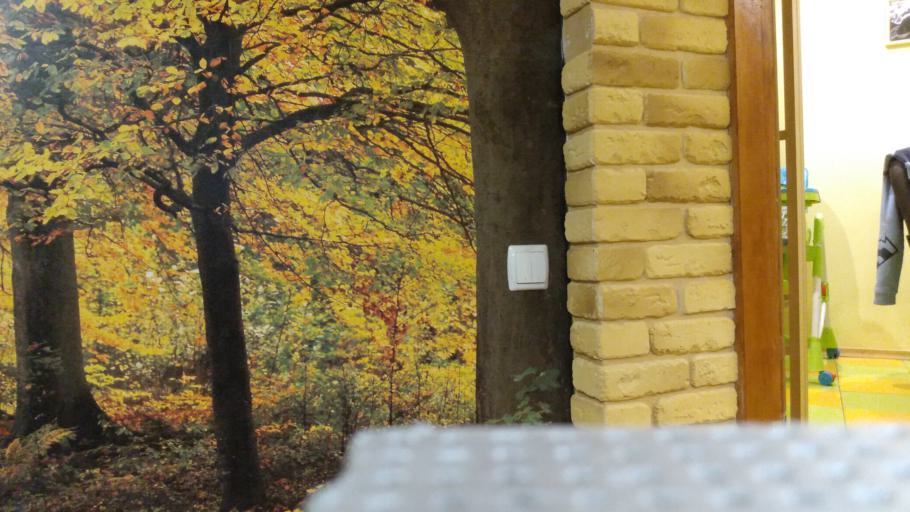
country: RU
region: Vologda
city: Babayevo
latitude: 59.3637
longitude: 36.0003
